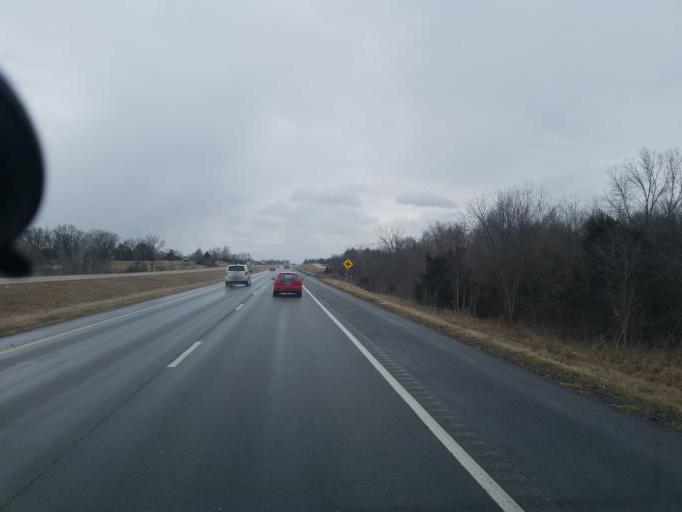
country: US
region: Missouri
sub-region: Randolph County
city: Moberly
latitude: 39.3678
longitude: -92.4071
